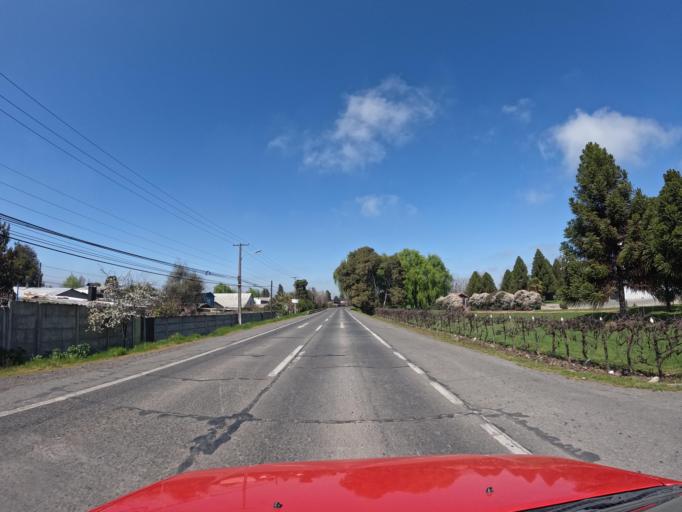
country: CL
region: Maule
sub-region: Provincia de Curico
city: Molina
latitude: -35.0666
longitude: -71.2559
